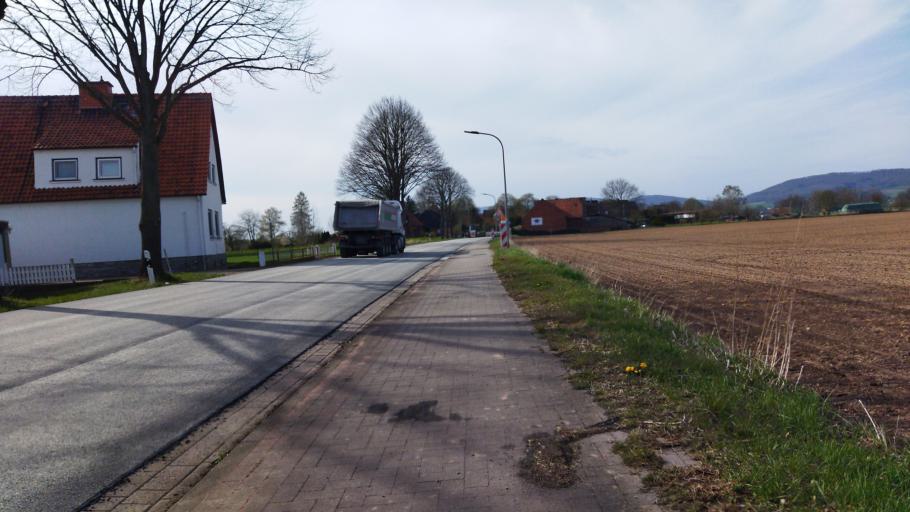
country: DE
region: Lower Saxony
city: Buchholz
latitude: 52.1757
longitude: 9.1681
